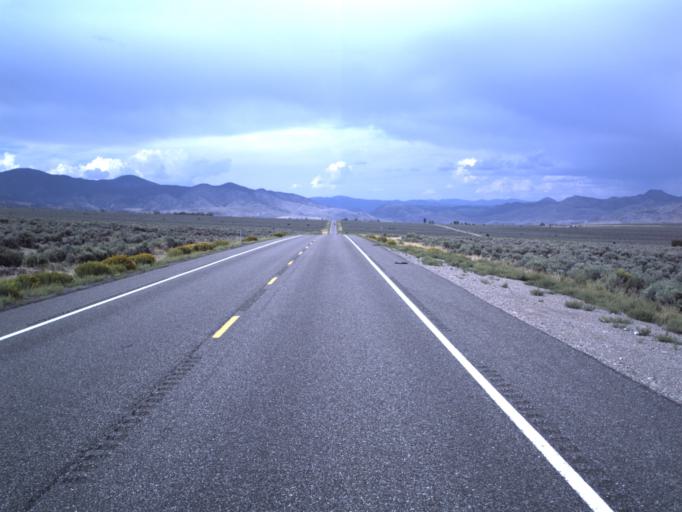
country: US
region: Utah
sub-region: Piute County
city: Junction
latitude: 38.3582
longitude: -112.2221
